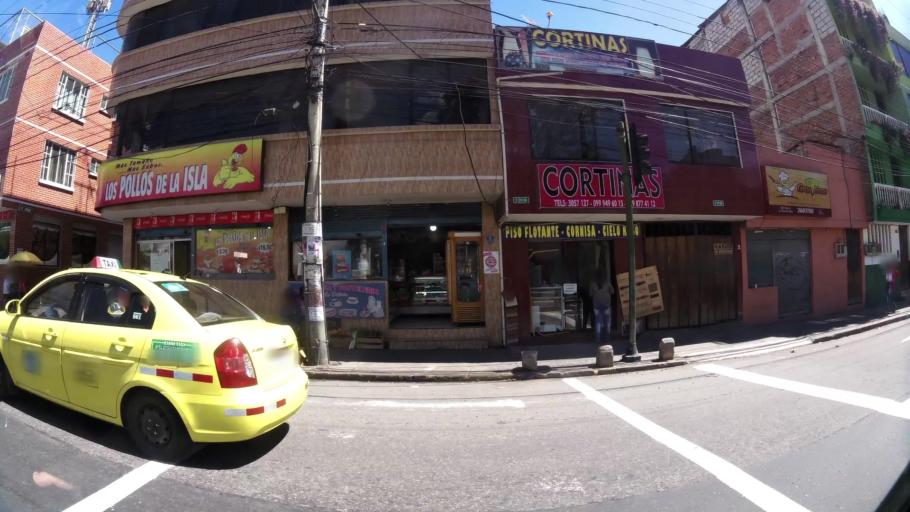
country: EC
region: Pichincha
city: Quito
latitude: -0.2681
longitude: -78.5464
